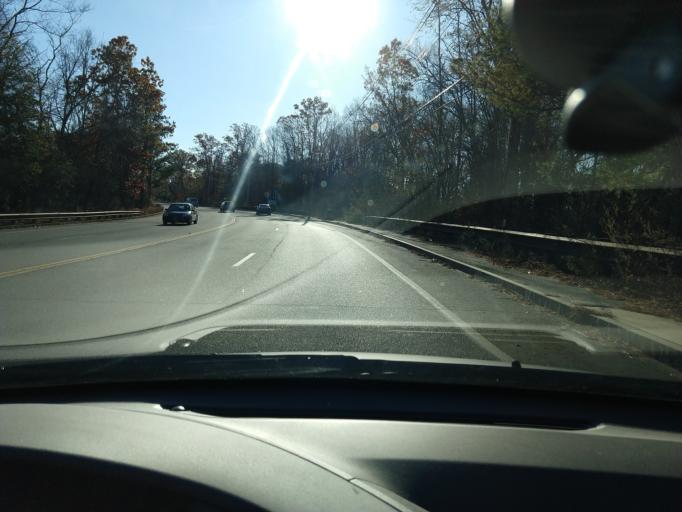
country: US
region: Massachusetts
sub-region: Middlesex County
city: Billerica
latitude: 42.5475
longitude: -71.2819
